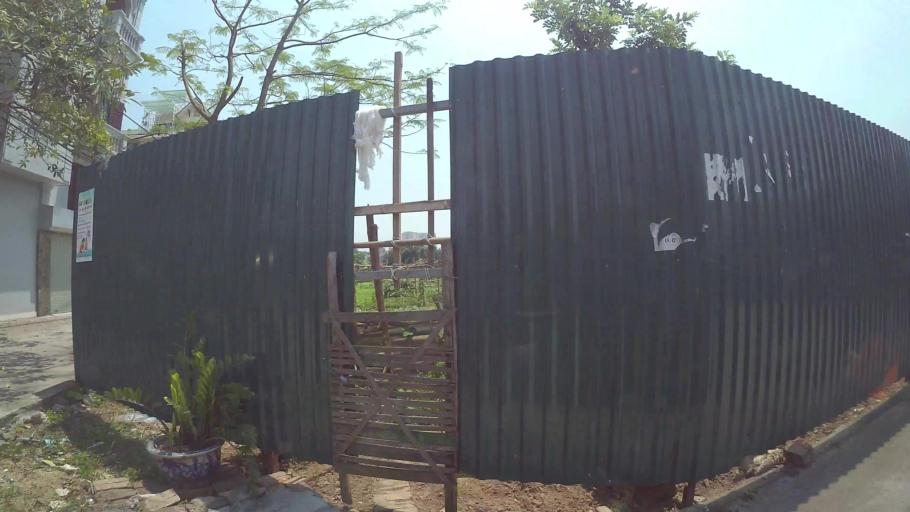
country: VN
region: Ha Noi
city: Trau Quy
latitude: 21.0287
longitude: 105.9084
